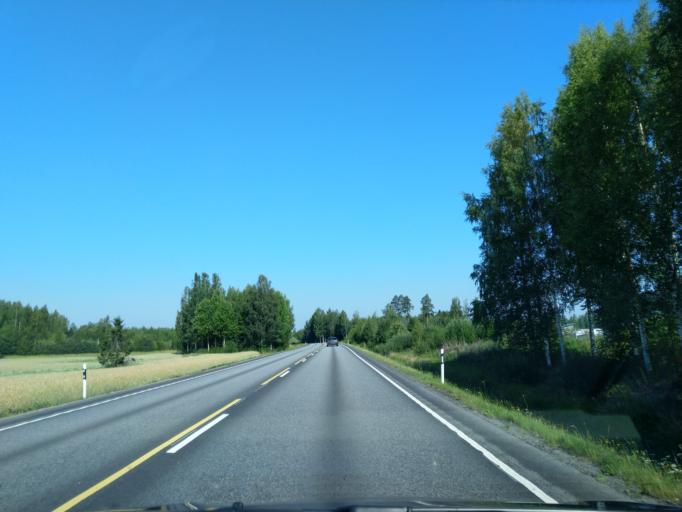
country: FI
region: Satakunta
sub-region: Pori
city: Huittinen
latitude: 61.1609
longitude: 22.7203
